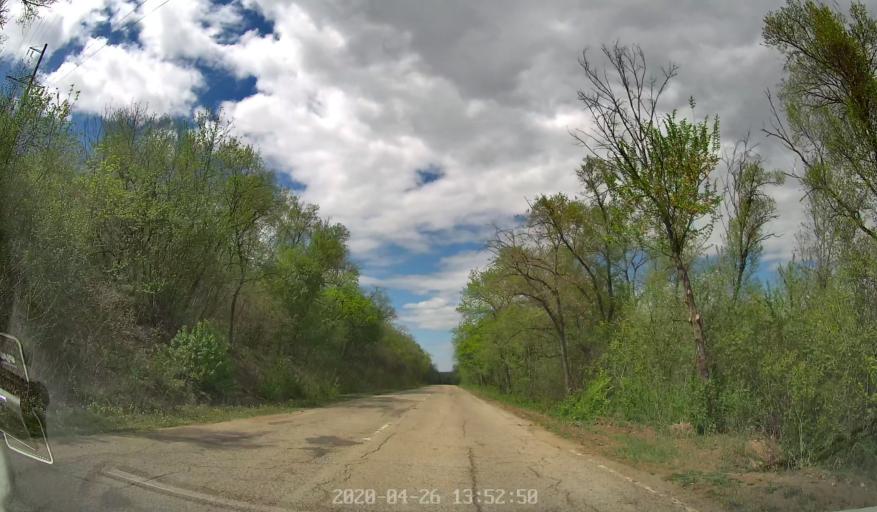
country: MD
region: Telenesti
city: Cocieri
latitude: 47.2748
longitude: 29.1151
